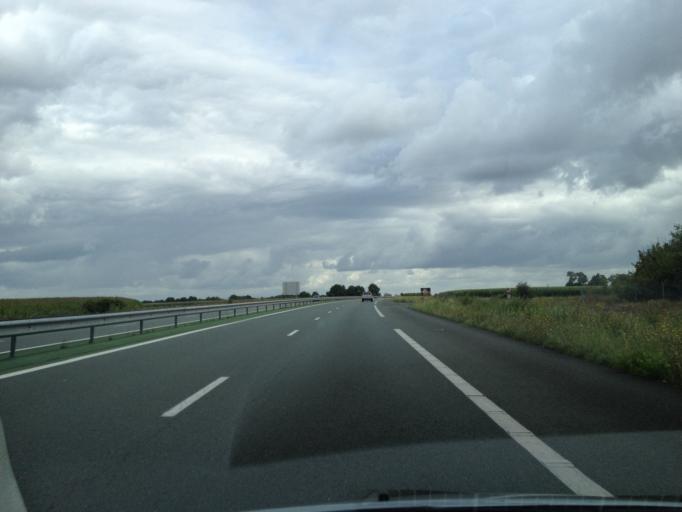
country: FR
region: Pays de la Loire
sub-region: Departement de la Vendee
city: Saint-Fulgent
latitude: 46.8574
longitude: -1.1430
